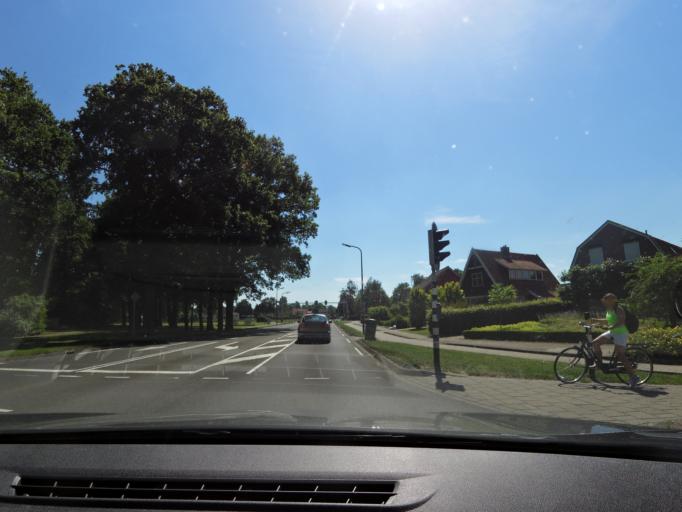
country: NL
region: Gelderland
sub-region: Berkelland
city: Eibergen
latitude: 52.0978
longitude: 6.6533
